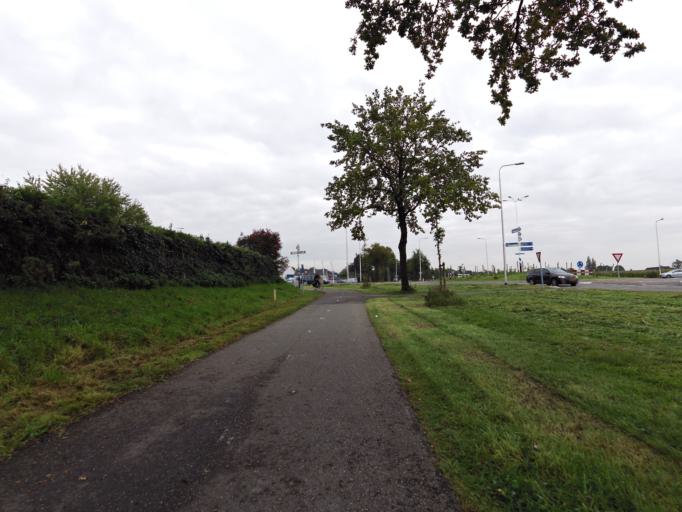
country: NL
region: Gelderland
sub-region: Oude IJsselstreek
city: Gendringen
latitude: 51.8885
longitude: 6.3676
